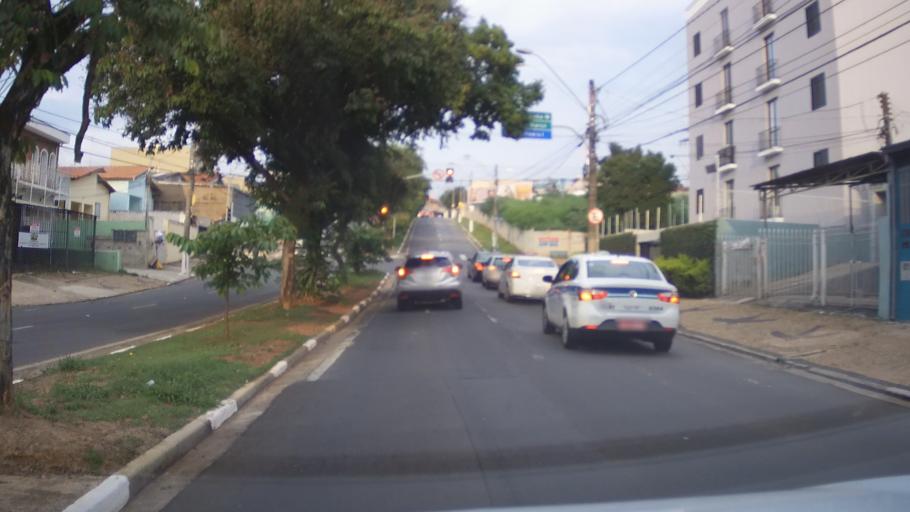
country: BR
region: Sao Paulo
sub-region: Campinas
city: Campinas
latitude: -22.8735
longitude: -47.0330
